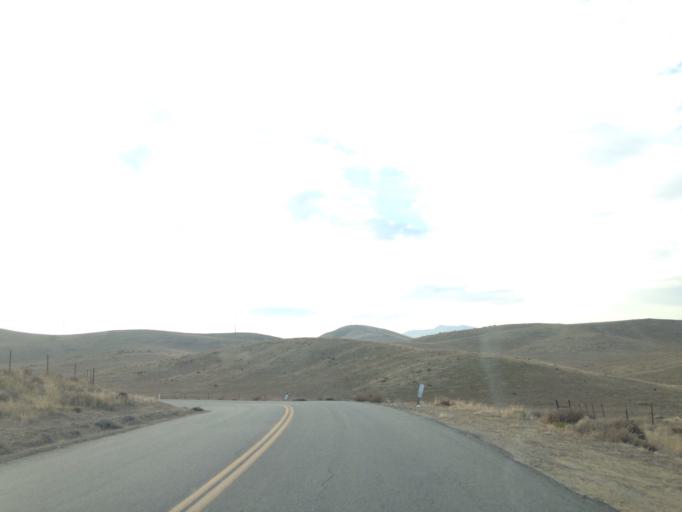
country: US
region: California
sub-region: Kings County
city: Kettleman City
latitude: 35.7280
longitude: -120.0178
